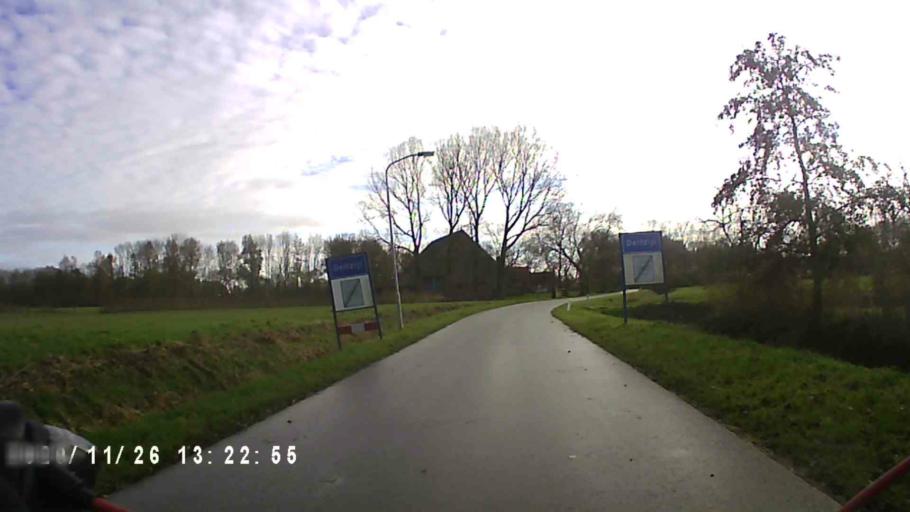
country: NL
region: Groningen
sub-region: Gemeente Delfzijl
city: Delfzijl
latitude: 53.3440
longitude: 6.8956
